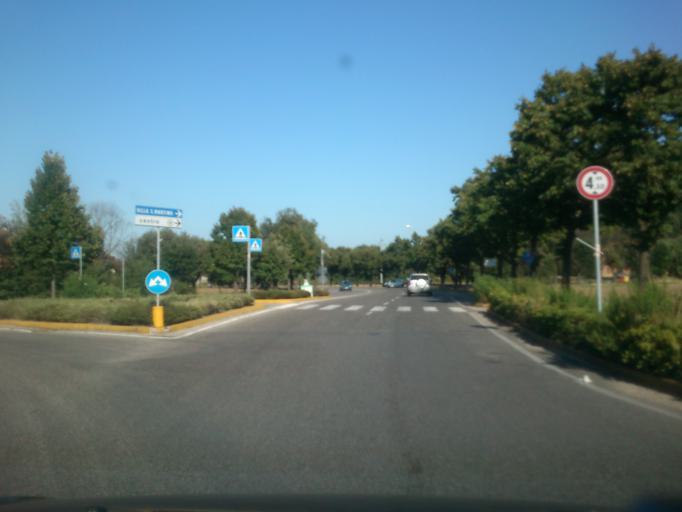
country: IT
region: The Marches
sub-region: Provincia di Pesaro e Urbino
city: Pesaro
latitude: 43.8899
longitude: 12.8844
